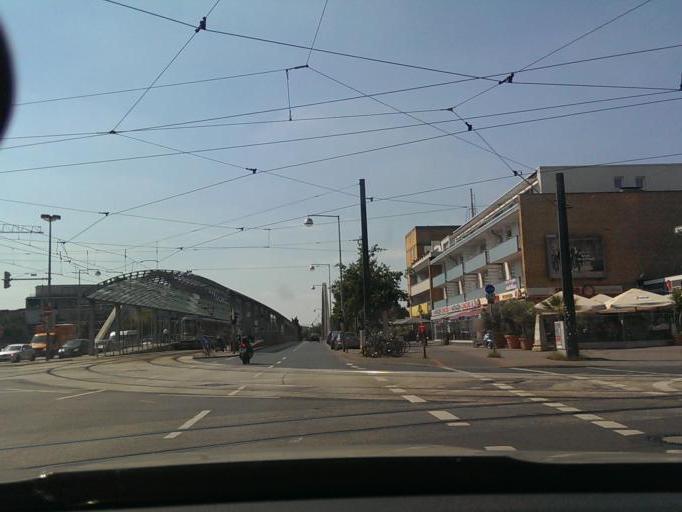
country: DE
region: Lower Saxony
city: Langenhagen
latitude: 52.4065
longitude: 9.8005
